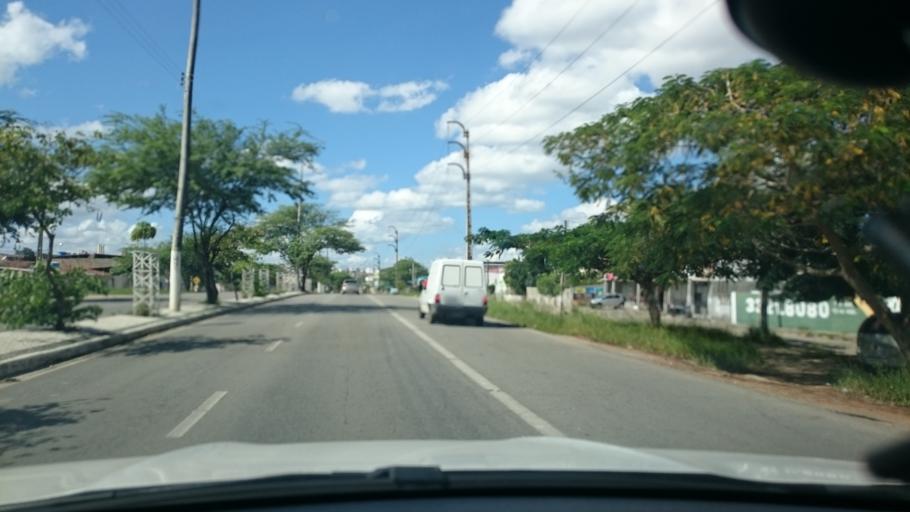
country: BR
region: Paraiba
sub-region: Campina Grande
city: Campina Grande
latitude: -7.2370
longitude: -35.9226
